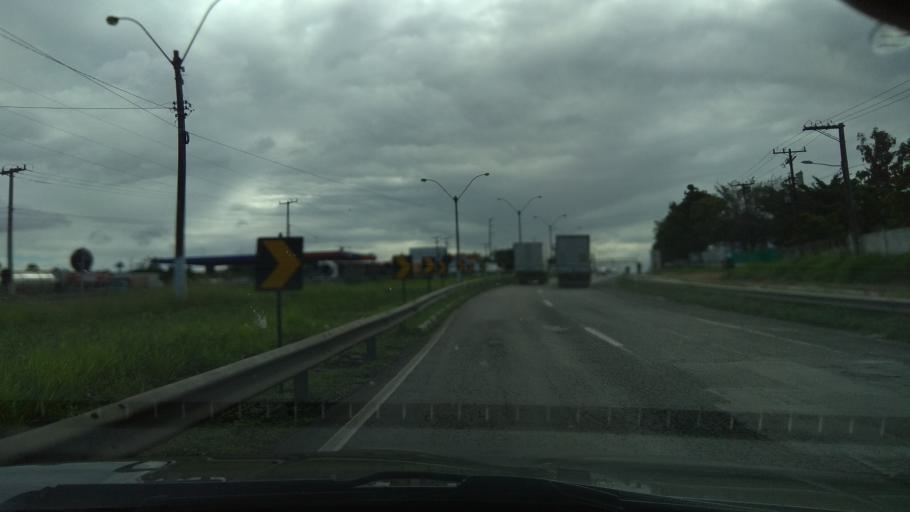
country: BR
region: Bahia
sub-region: Feira De Santana
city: Feira de Santana
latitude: -12.2983
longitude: -38.9009
